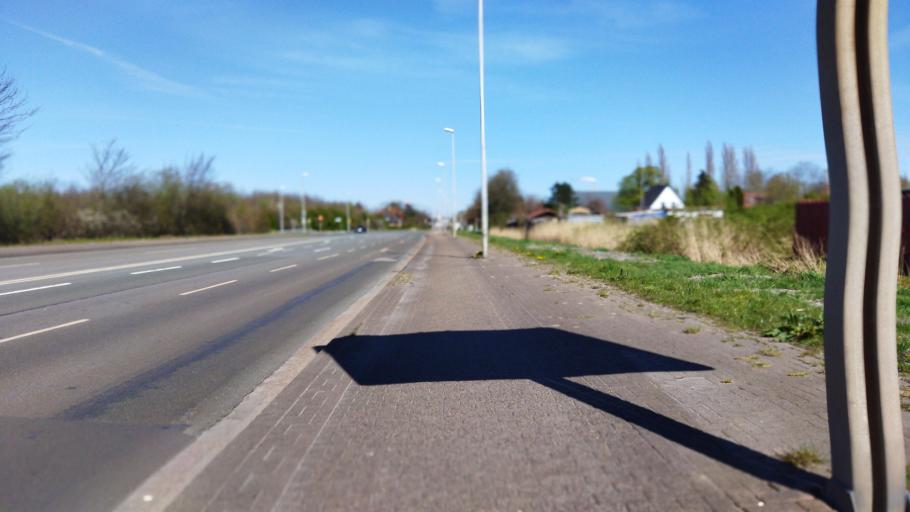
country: DE
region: Lower Saxony
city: Nordenham
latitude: 53.5209
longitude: 8.5164
